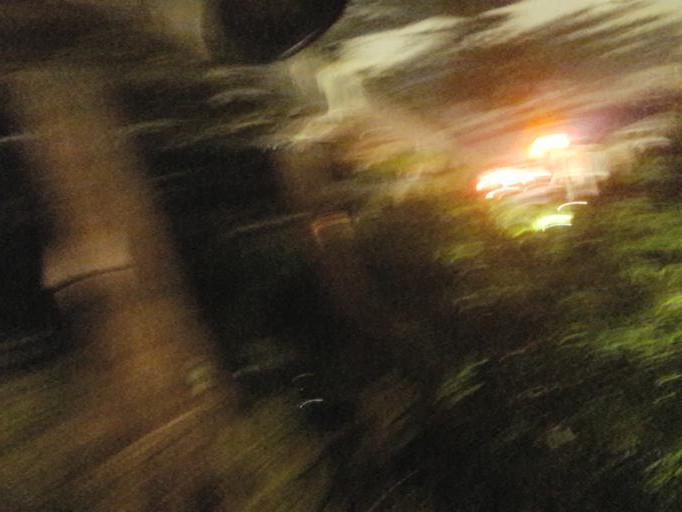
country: IN
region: Telangana
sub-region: Rangareddi
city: Kukatpalli
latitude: 17.4805
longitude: 78.3924
